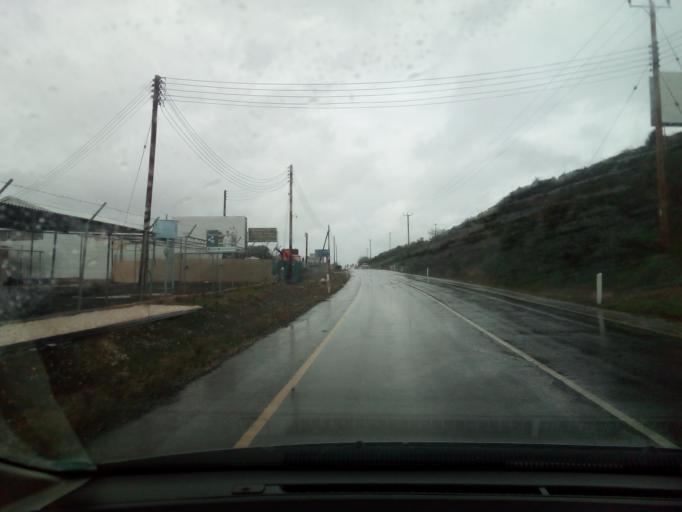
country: CY
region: Pafos
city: Polis
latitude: 34.9906
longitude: 32.4506
